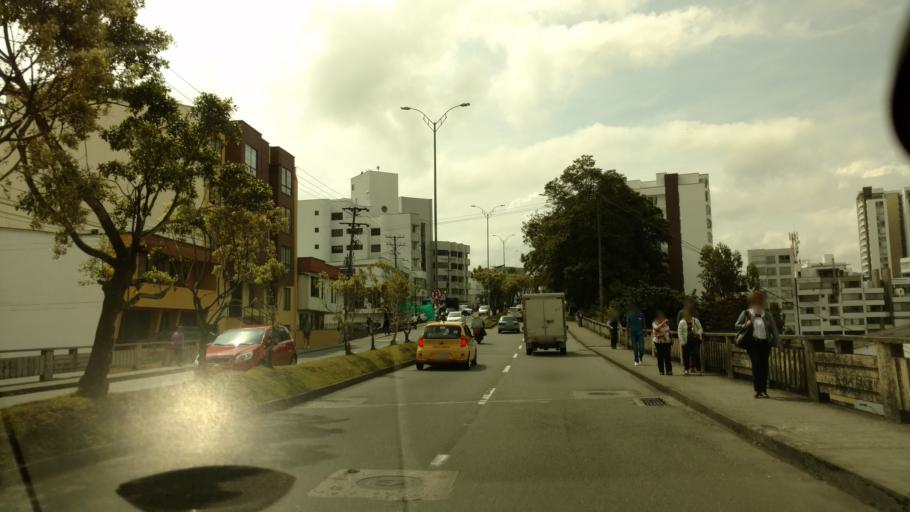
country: CO
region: Caldas
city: Villamaria
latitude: 5.0547
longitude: -75.4847
